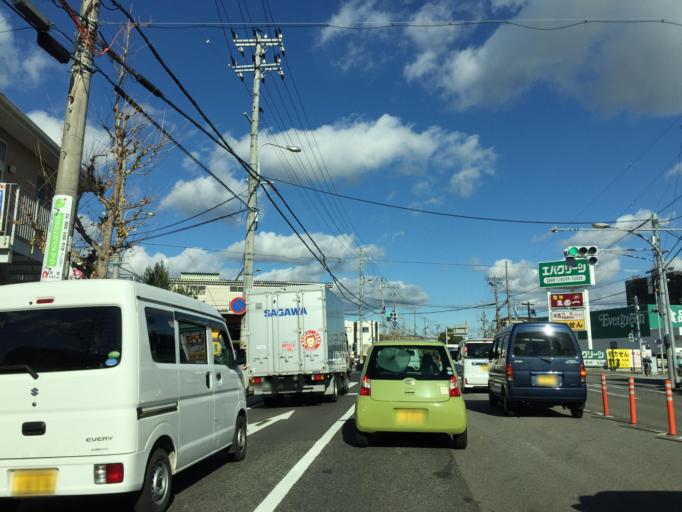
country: JP
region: Wakayama
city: Wakayama-shi
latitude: 34.2003
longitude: 135.1780
